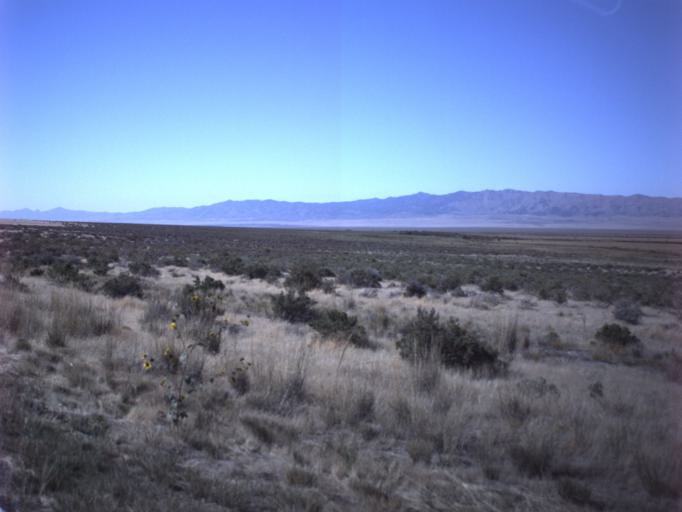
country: US
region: Utah
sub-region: Tooele County
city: Grantsville
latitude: 40.6132
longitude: -112.7046
